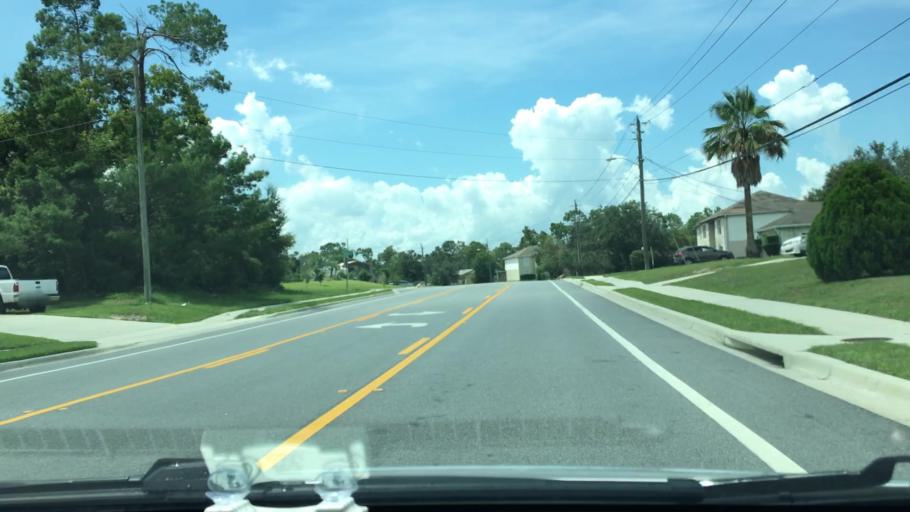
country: US
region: Florida
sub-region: Volusia County
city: Deltona
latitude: 28.8793
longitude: -81.1615
